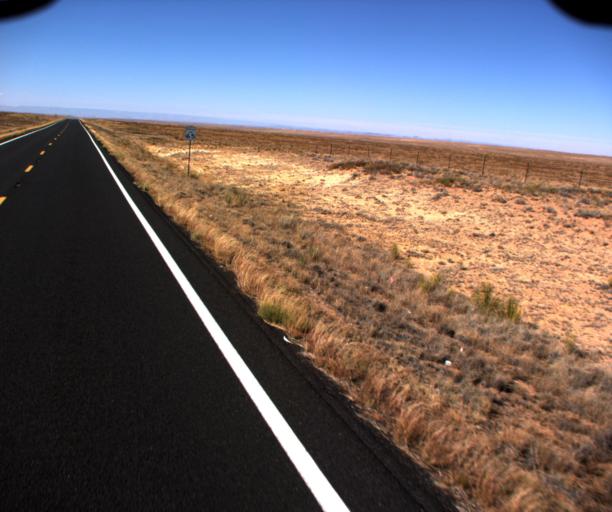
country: US
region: Arizona
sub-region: Coconino County
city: Tuba City
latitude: 36.0104
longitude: -111.0680
